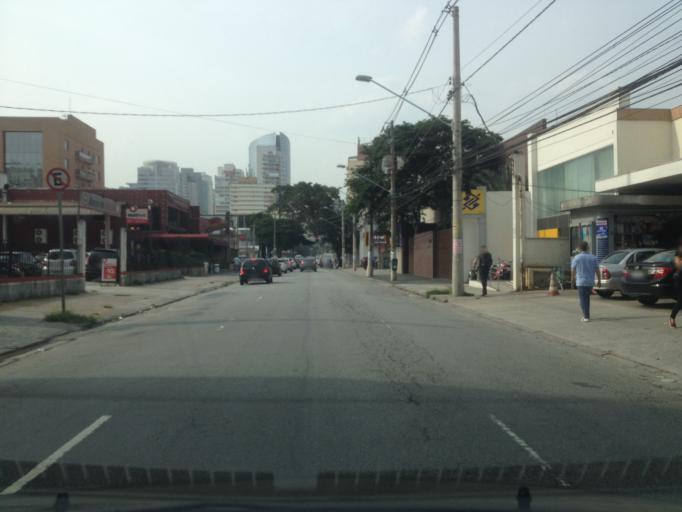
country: BR
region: Sao Paulo
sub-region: Sao Paulo
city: Sao Paulo
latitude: -23.5927
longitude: -46.6775
